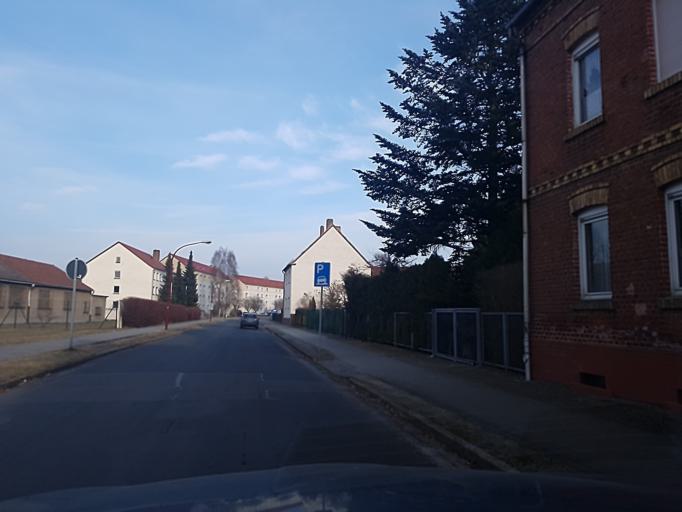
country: DE
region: Brandenburg
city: Finsterwalde
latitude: 51.6332
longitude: 13.7171
